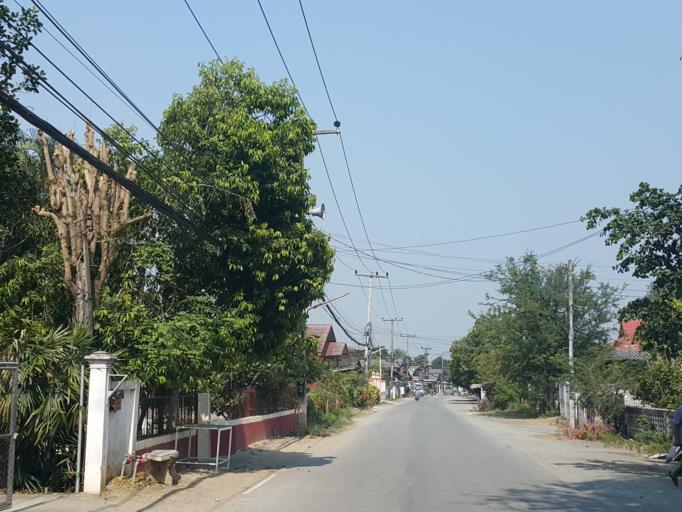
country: TH
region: Chiang Mai
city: San Kamphaeng
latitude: 18.7376
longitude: 99.1085
